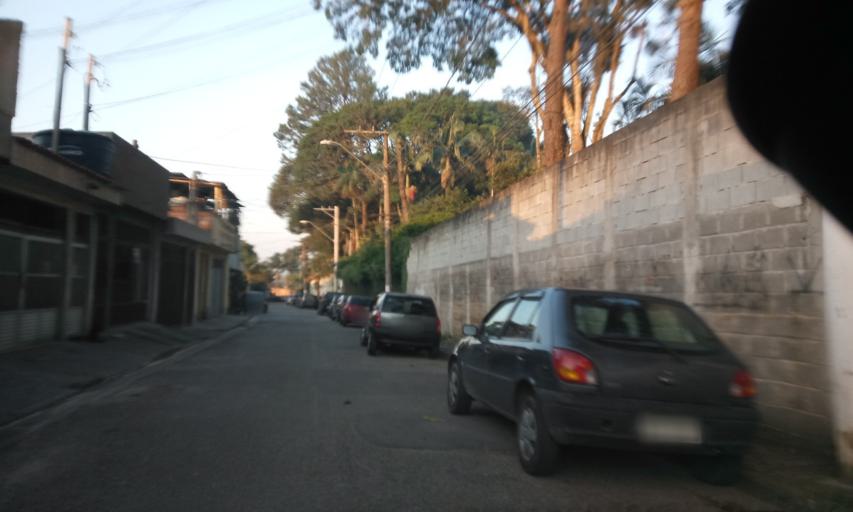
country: BR
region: Sao Paulo
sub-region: Sao Bernardo Do Campo
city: Sao Bernardo do Campo
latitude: -23.7951
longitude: -46.5451
